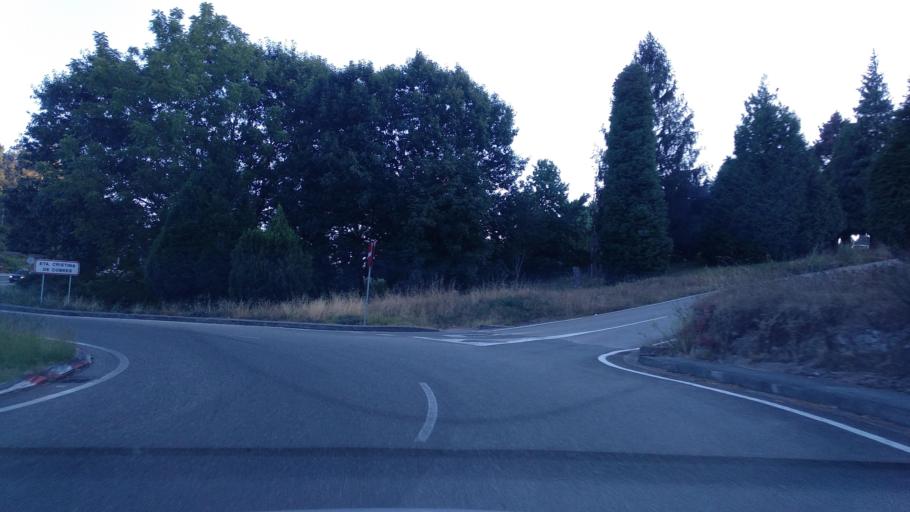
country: ES
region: Galicia
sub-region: Provincia de Pontevedra
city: Redondela
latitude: 42.3334
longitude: -8.6466
